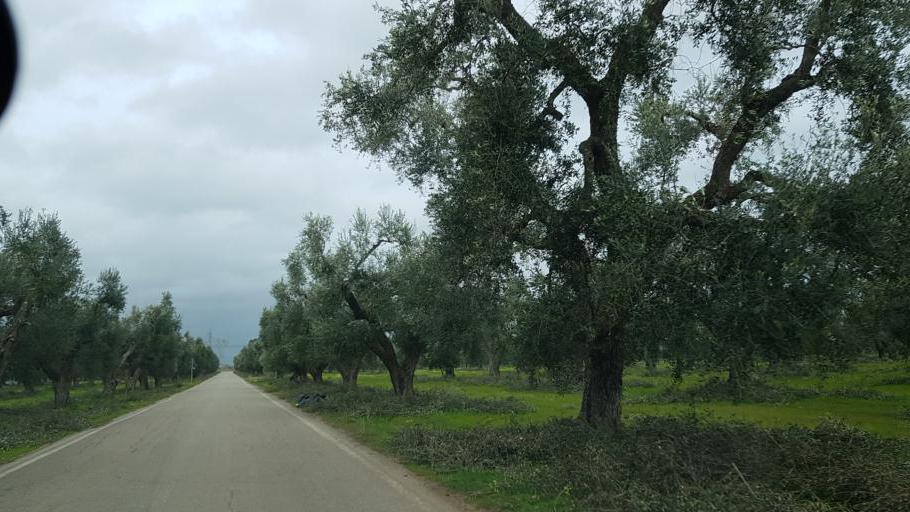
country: IT
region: Apulia
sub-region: Provincia di Brindisi
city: Brindisi
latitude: 40.5959
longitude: 17.9003
